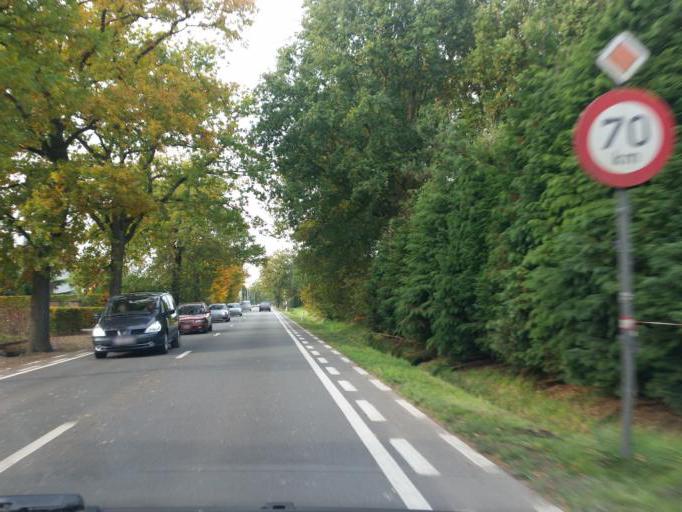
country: BE
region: Flanders
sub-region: Provincie Antwerpen
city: Heist-op-den-Berg
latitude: 51.0709
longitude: 4.6926
